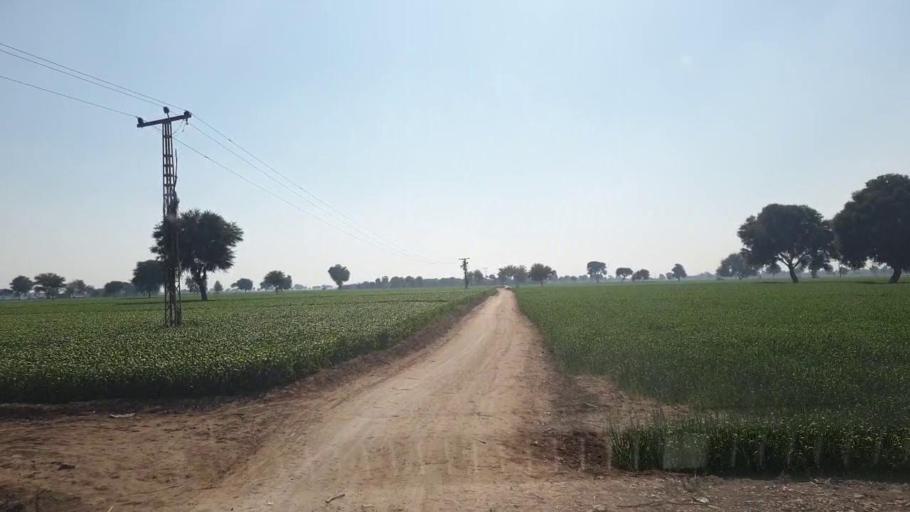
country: PK
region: Sindh
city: Shahpur Chakar
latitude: 26.1008
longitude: 68.6328
